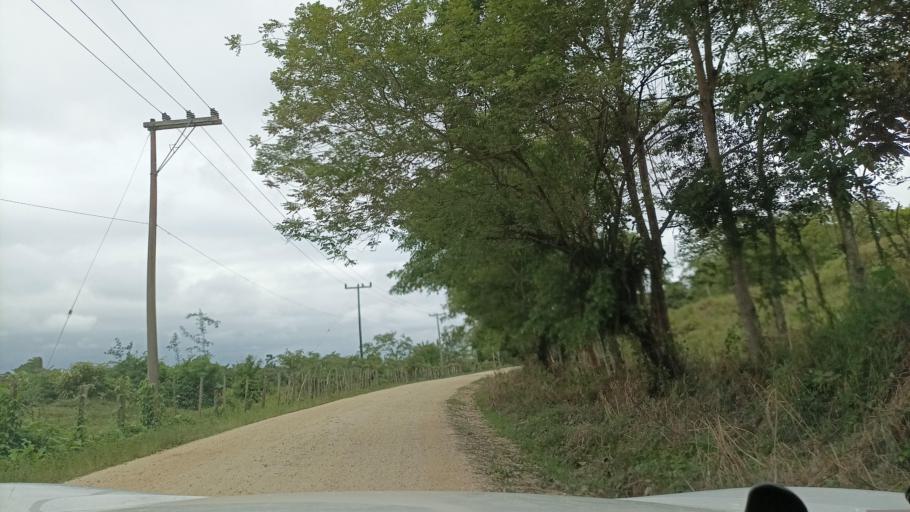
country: MX
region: Veracruz
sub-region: Moloacan
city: Cuichapa
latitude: 17.8383
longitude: -94.3566
